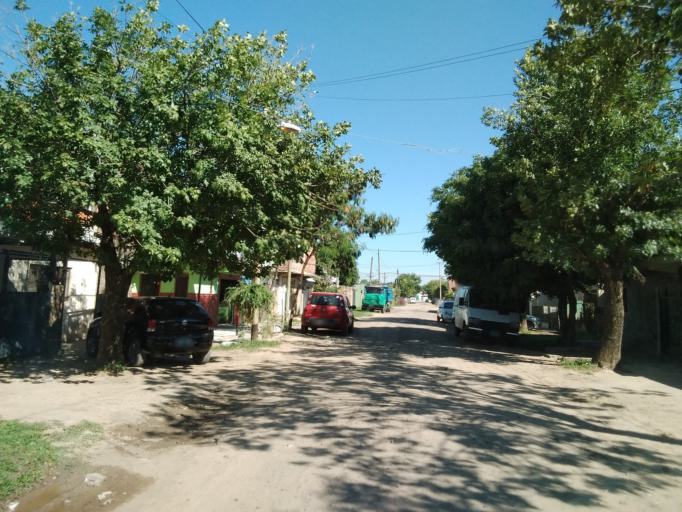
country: AR
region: Corrientes
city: Corrientes
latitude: -27.4845
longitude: -58.8095
